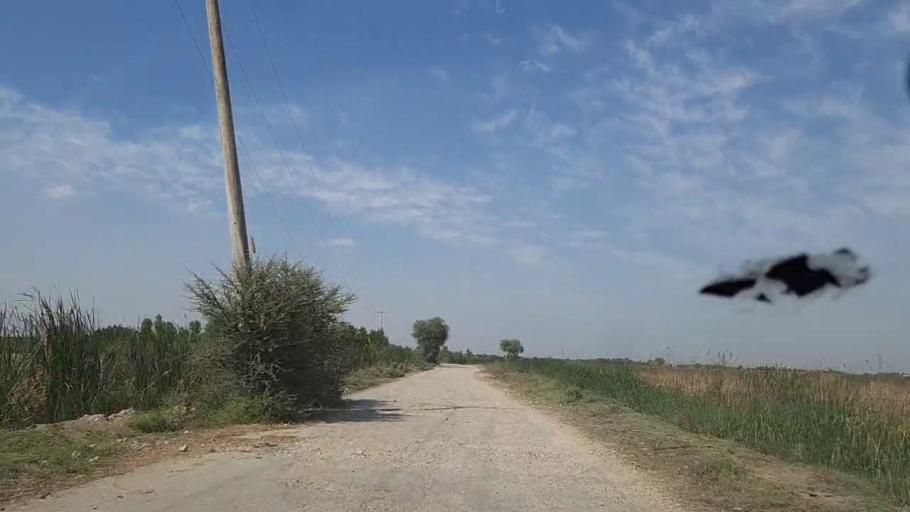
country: PK
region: Sindh
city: Thatta
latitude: 24.6375
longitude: 68.0762
